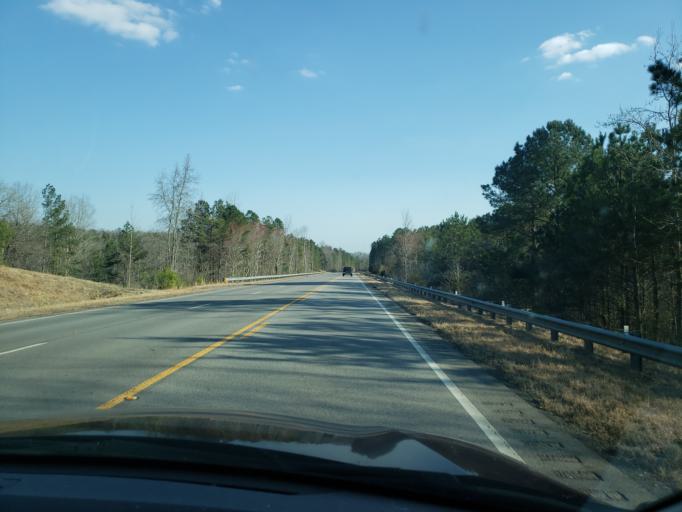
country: US
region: Alabama
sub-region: Randolph County
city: Wedowee
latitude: 33.4411
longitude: -85.5638
